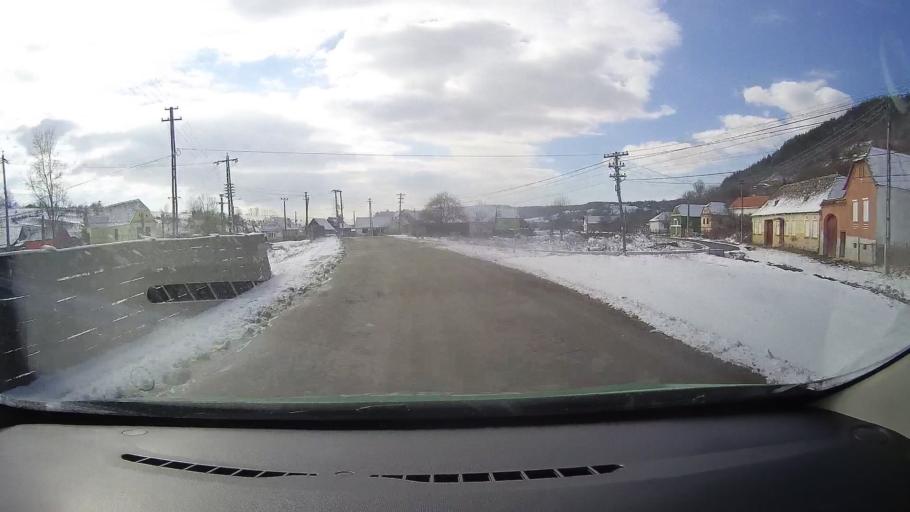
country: RO
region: Sibiu
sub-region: Comuna Mihaileni
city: Mihaileni
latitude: 46.0094
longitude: 24.3703
